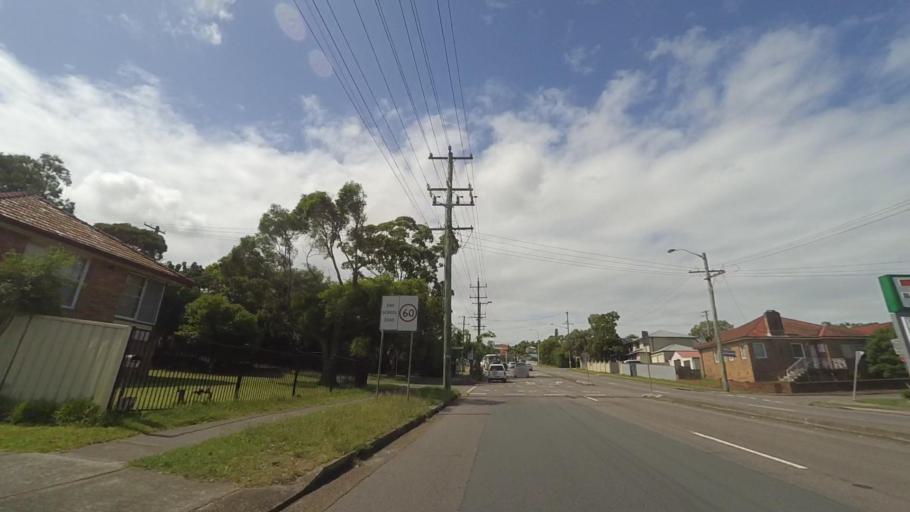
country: AU
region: New South Wales
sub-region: Newcastle
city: North Lambton
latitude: -32.9106
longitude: 151.7050
